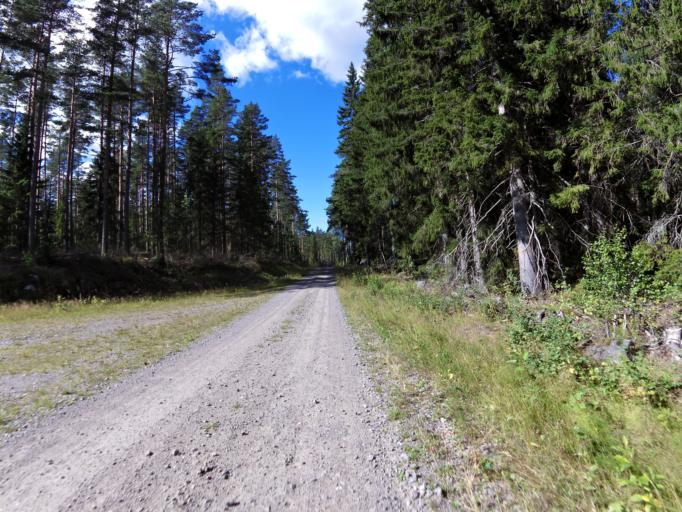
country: SE
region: Gaevleborg
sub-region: Ockelbo Kommun
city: Ockelbo
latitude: 60.8070
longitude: 16.7973
